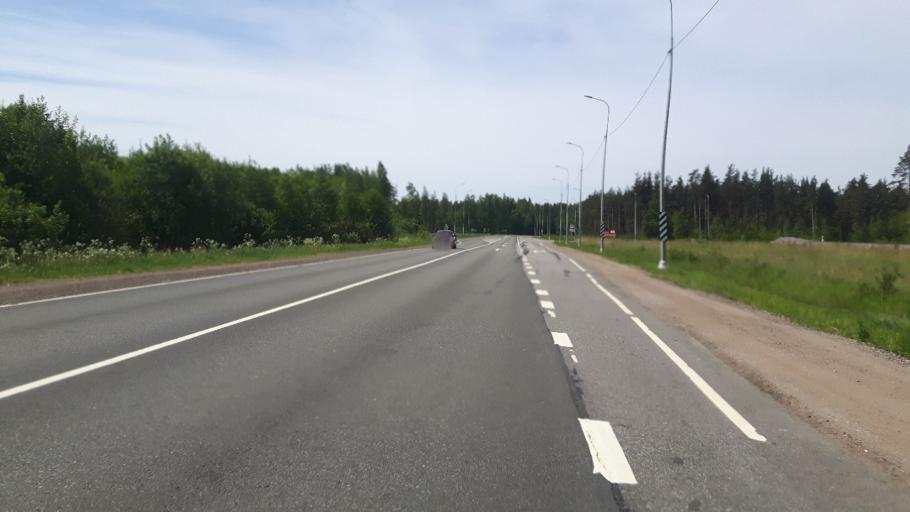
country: RU
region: Leningrad
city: Ust'-Luga
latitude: 59.6522
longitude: 28.3718
